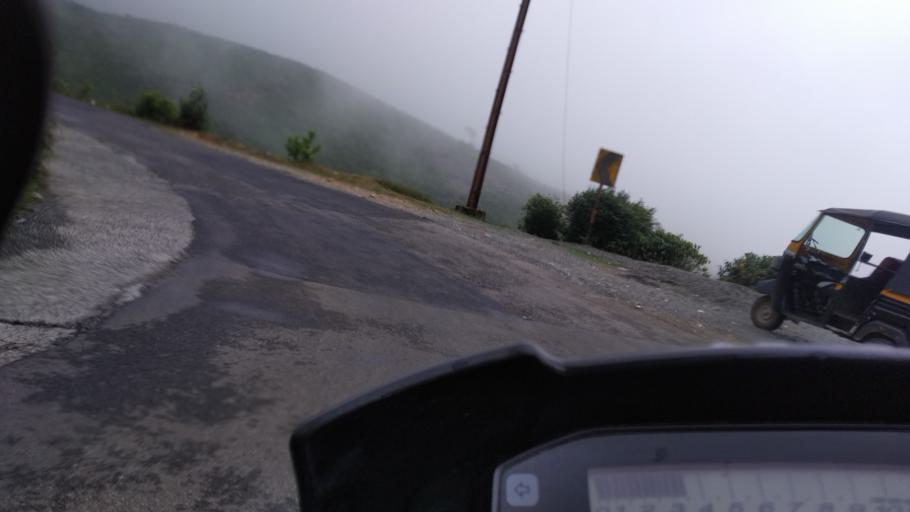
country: IN
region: Kerala
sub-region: Kottayam
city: Erattupetta
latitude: 9.6331
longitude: 76.9385
